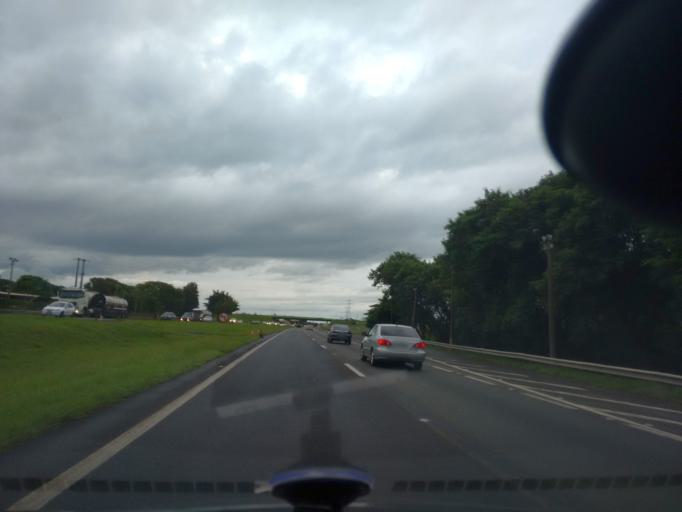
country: BR
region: Sao Paulo
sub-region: Rio Claro
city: Rio Claro
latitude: -22.4389
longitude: -47.5677
